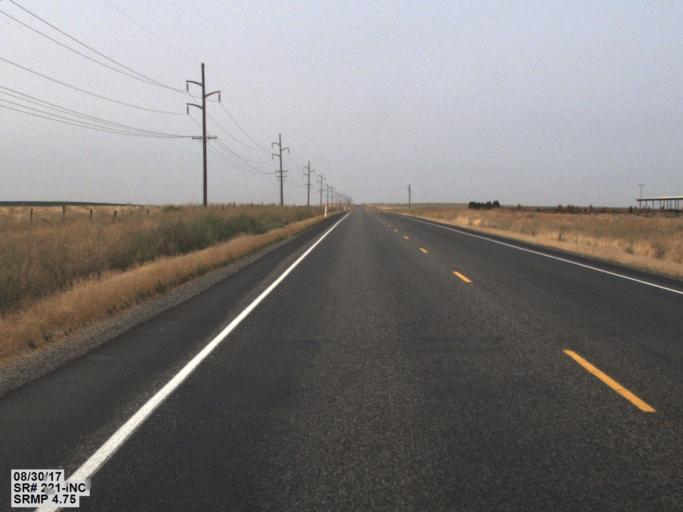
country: US
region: Oregon
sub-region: Morrow County
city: Irrigon
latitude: 46.0039
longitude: -119.6028
